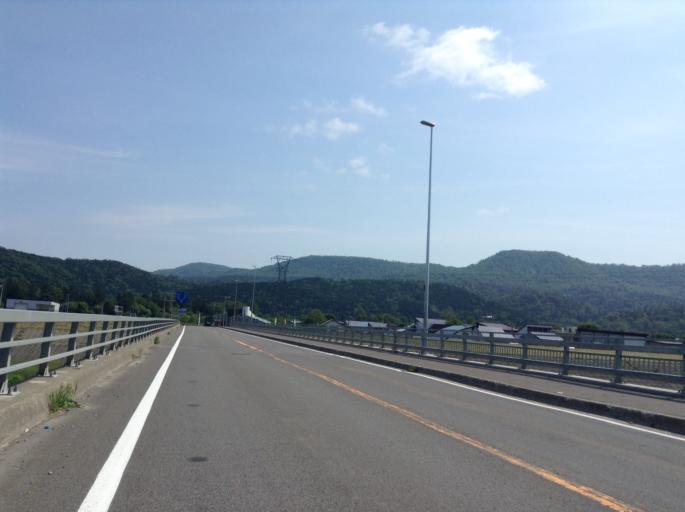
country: JP
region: Hokkaido
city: Nayoro
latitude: 44.7271
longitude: 142.2549
